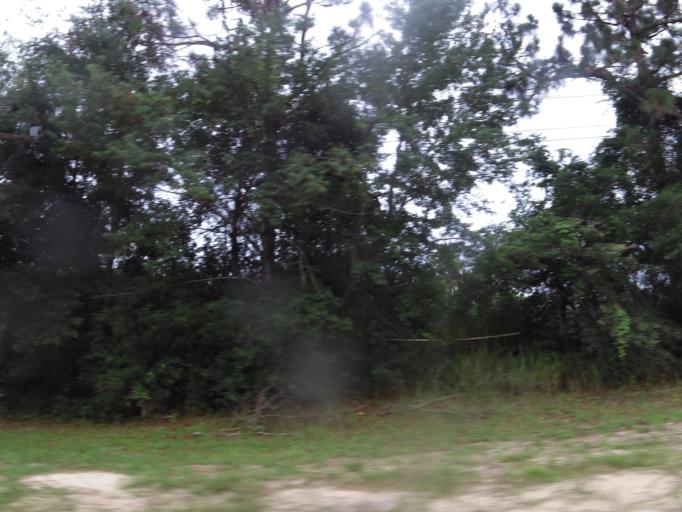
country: US
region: Florida
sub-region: Duval County
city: Jacksonville
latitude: 30.2648
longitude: -81.5417
